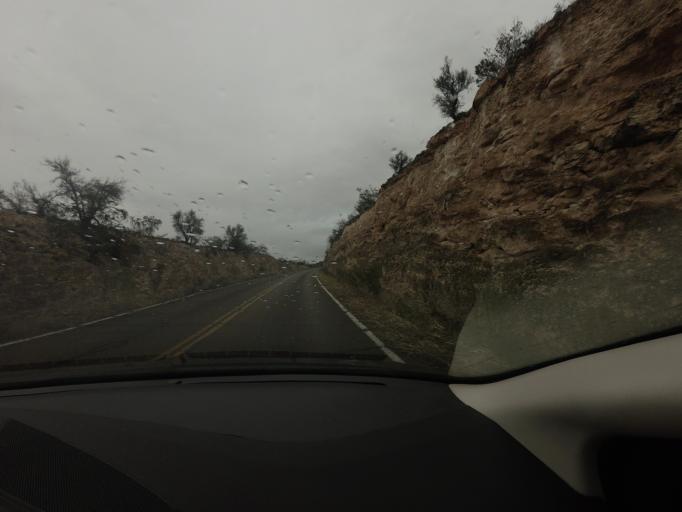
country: US
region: Arizona
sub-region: Yavapai County
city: Camp Verde
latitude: 34.6106
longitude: -111.8511
